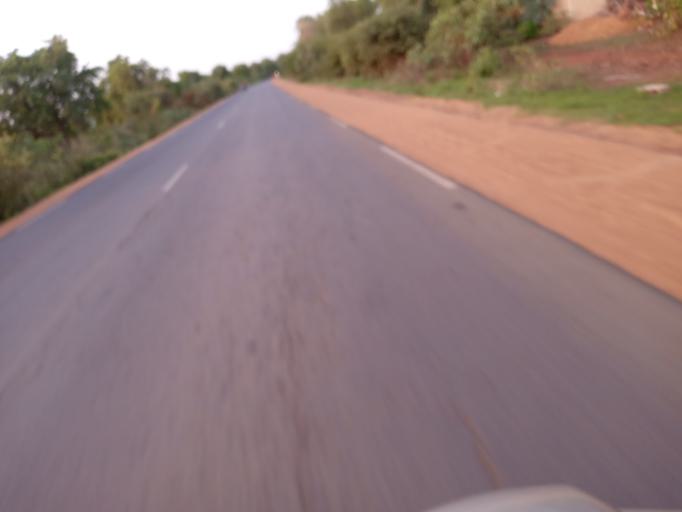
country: ML
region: Bamako
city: Bamako
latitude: 12.2841
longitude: -8.1763
